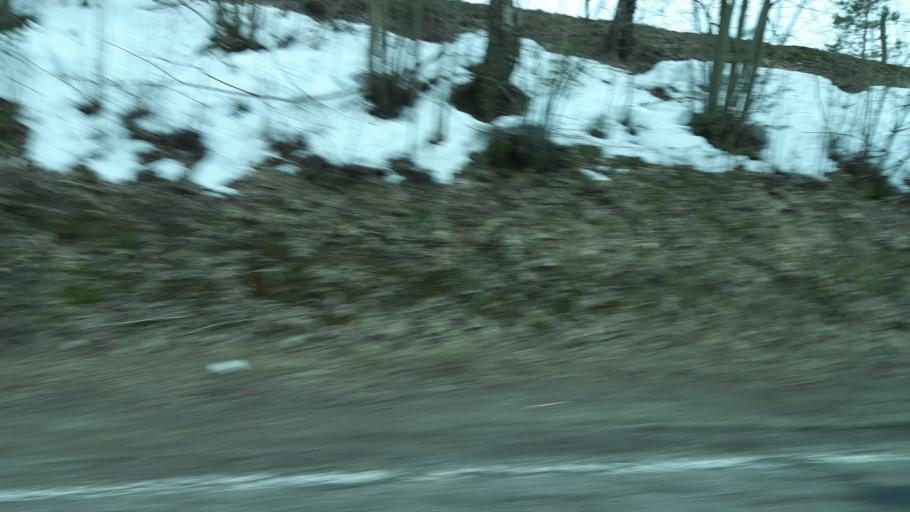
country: PL
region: Podlasie
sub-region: Suwalki
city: Suwalki
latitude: 54.3290
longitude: 22.9603
